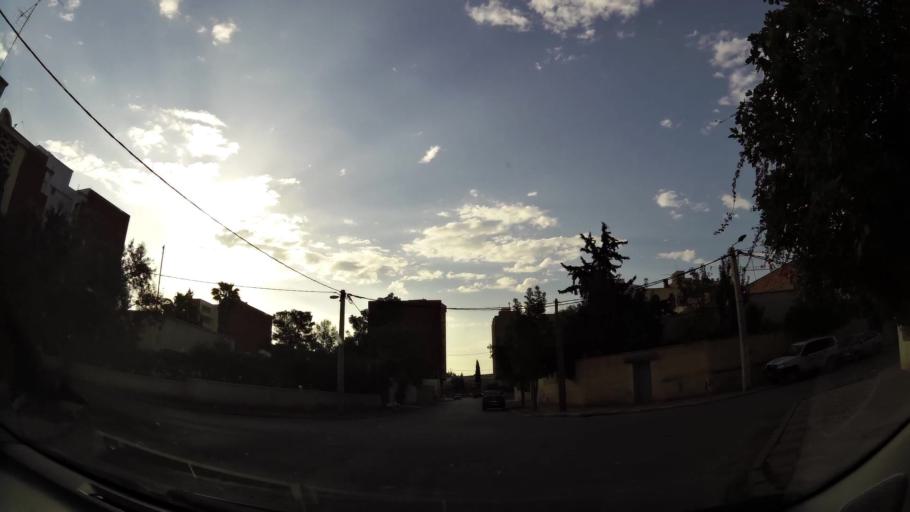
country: MA
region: Oriental
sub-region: Oujda-Angad
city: Oujda
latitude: 34.6770
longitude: -1.9238
